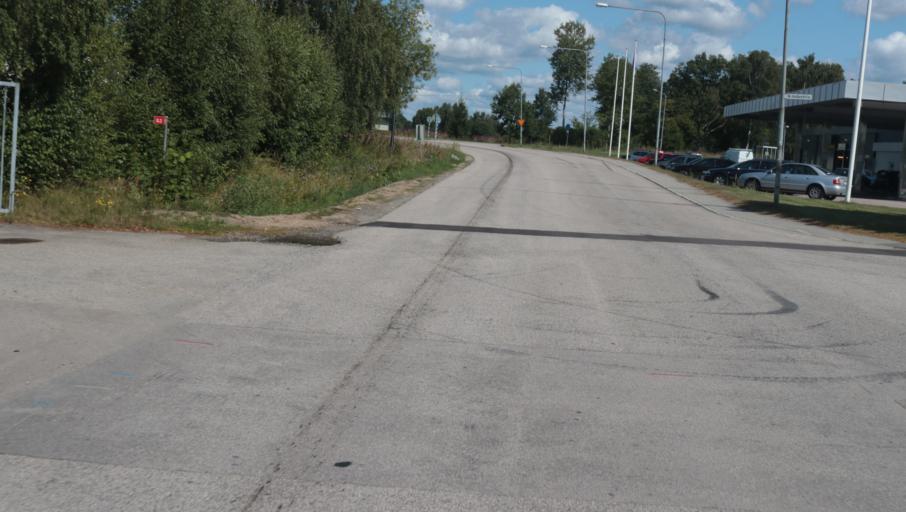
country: SE
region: Blekinge
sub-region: Karlshamns Kommun
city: Karlshamn
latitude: 56.2000
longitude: 14.8183
